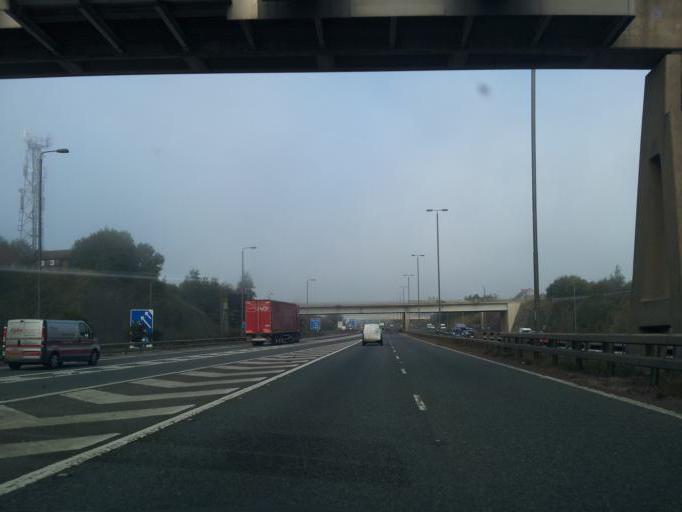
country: GB
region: England
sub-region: City and Borough of Leeds
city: Lofthouse
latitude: 53.7323
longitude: -1.5192
